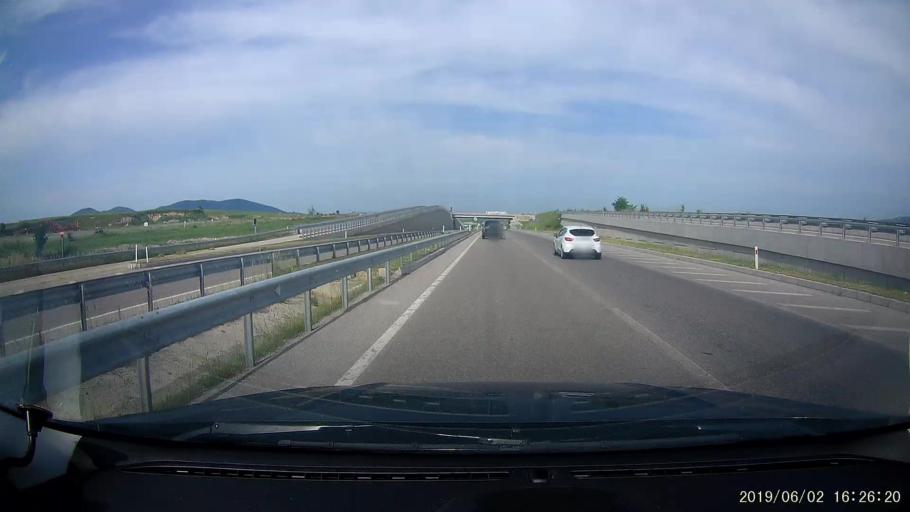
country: TR
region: Samsun
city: Ladik
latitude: 40.9991
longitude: 35.7995
